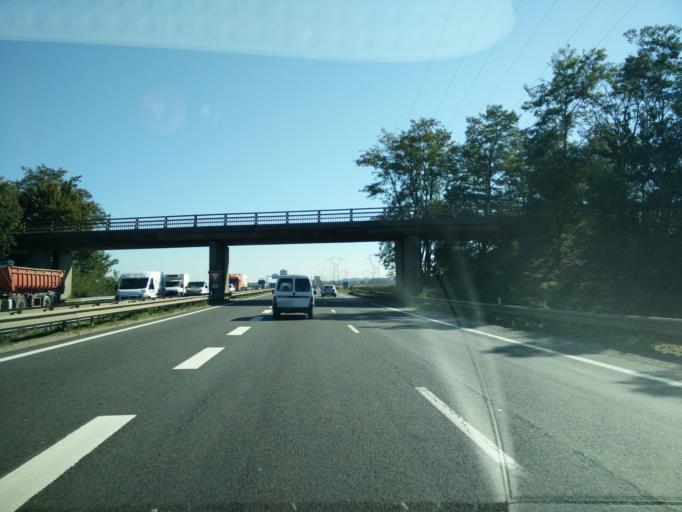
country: FR
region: Ile-de-France
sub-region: Departement de Seine-et-Marne
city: Mitry-Mory
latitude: 48.9736
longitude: 2.5894
